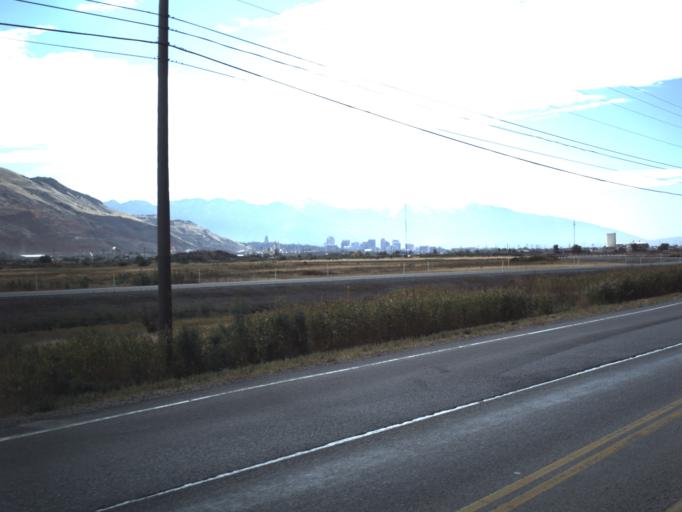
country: US
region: Utah
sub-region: Davis County
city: North Salt Lake
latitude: 40.8259
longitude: -111.9375
